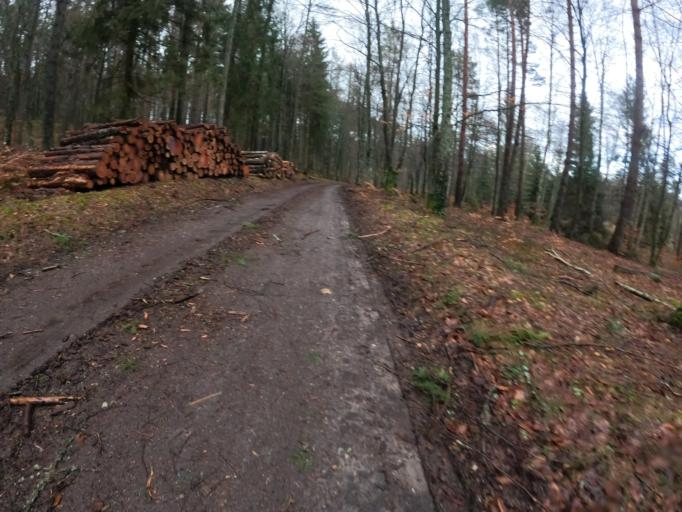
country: PL
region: West Pomeranian Voivodeship
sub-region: Powiat slawienski
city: Slawno
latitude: 54.2638
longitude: 16.7125
